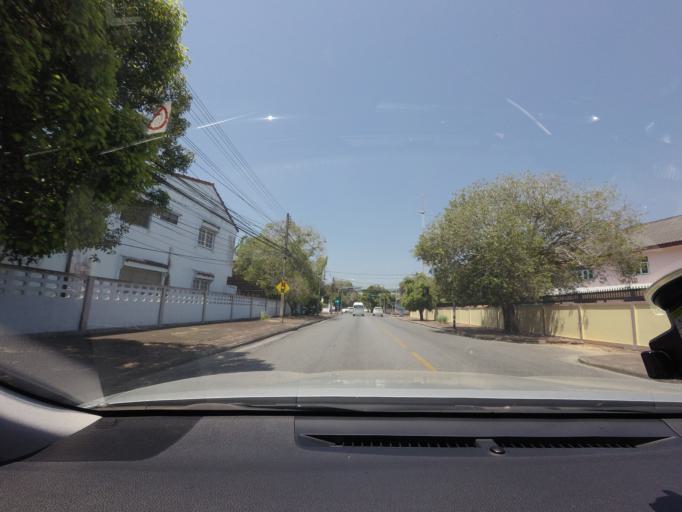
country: TH
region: Yala
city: Yala
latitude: 6.5410
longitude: 101.2832
